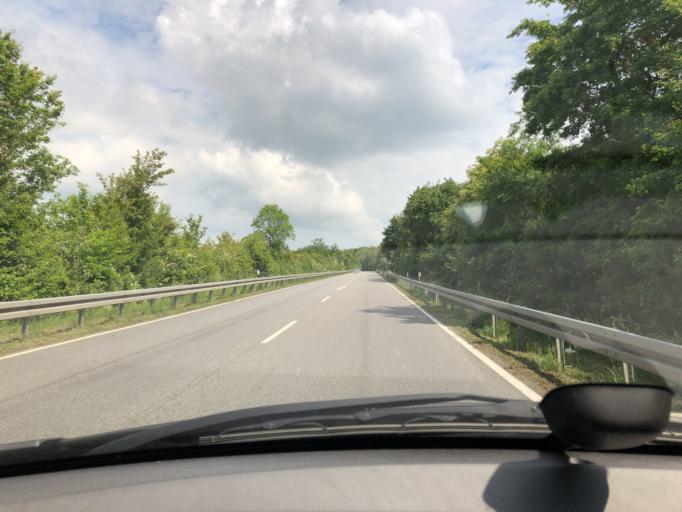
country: DE
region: Saarland
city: Kleinblittersdorf
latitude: 49.1666
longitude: 7.0410
